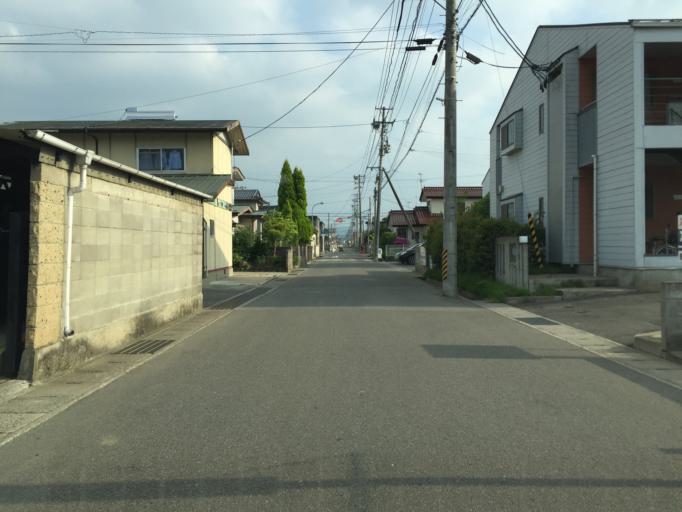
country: JP
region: Fukushima
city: Fukushima-shi
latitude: 37.7368
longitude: 140.4509
